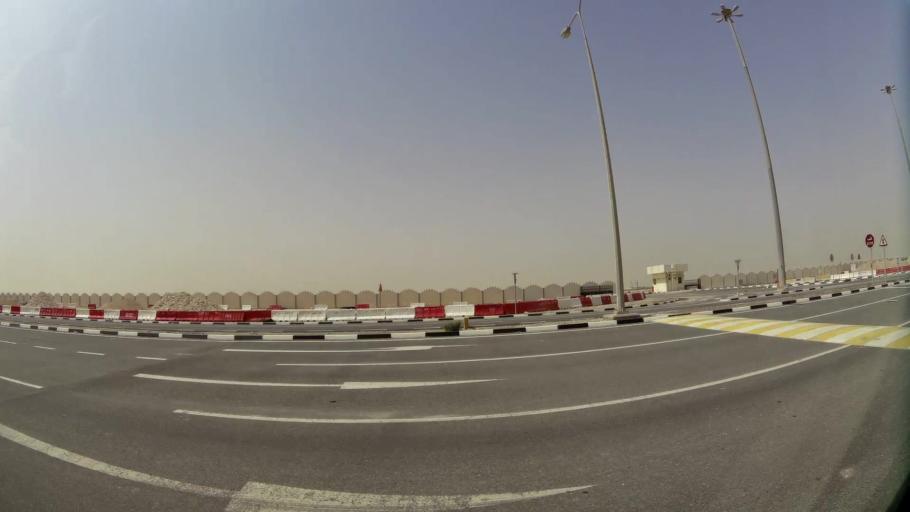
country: QA
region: Al Wakrah
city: Al Wukayr
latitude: 25.1487
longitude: 51.3909
